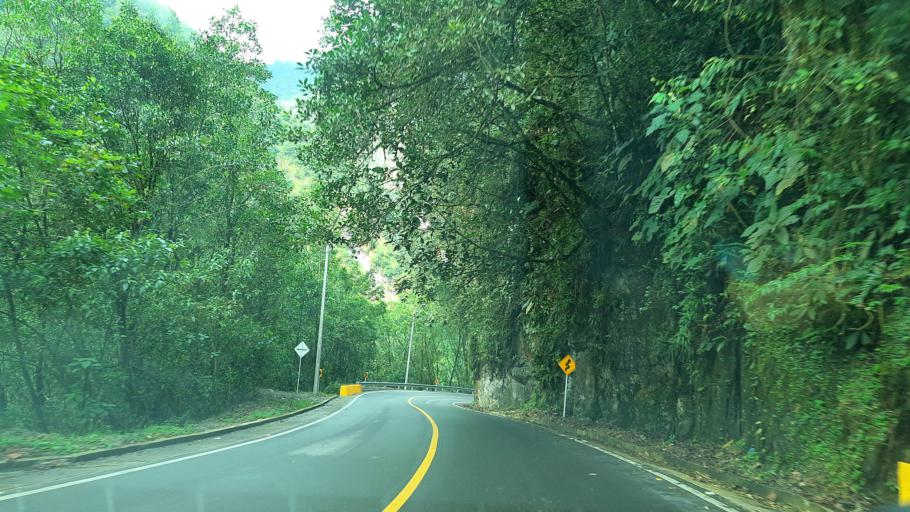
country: CO
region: Boyaca
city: Santa Maria
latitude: 4.8939
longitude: -73.2887
